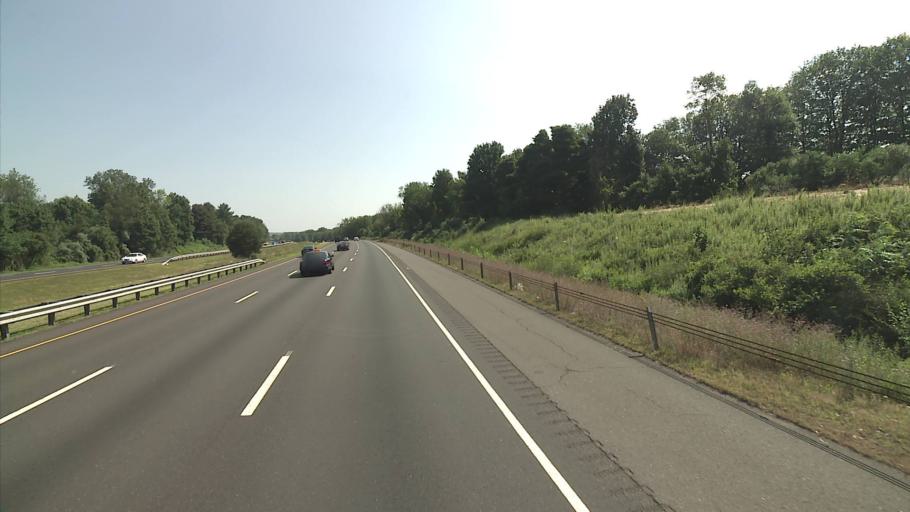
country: US
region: Connecticut
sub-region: New Haven County
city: Wallingford Center
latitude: 41.4357
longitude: -72.7999
